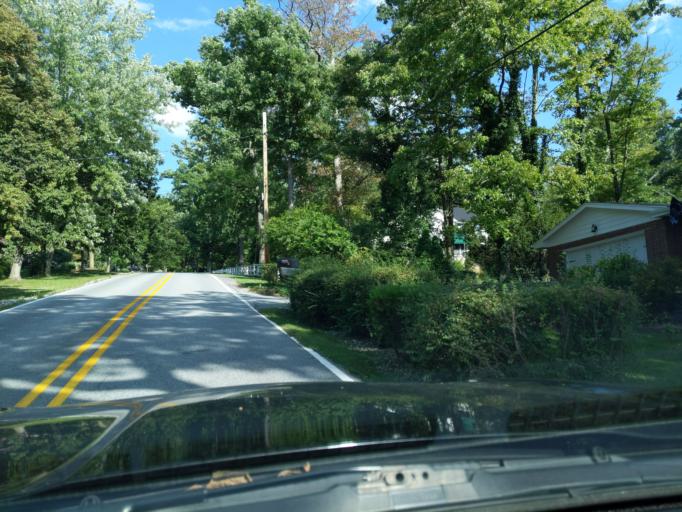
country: US
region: Pennsylvania
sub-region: Blair County
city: Hollidaysburg
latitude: 40.4488
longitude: -78.3927
